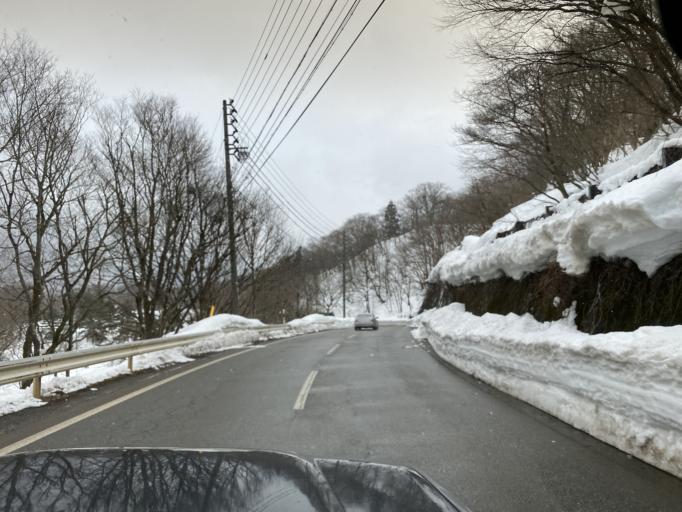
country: JP
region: Toyama
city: Fukumitsu
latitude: 36.2113
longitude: 136.8919
